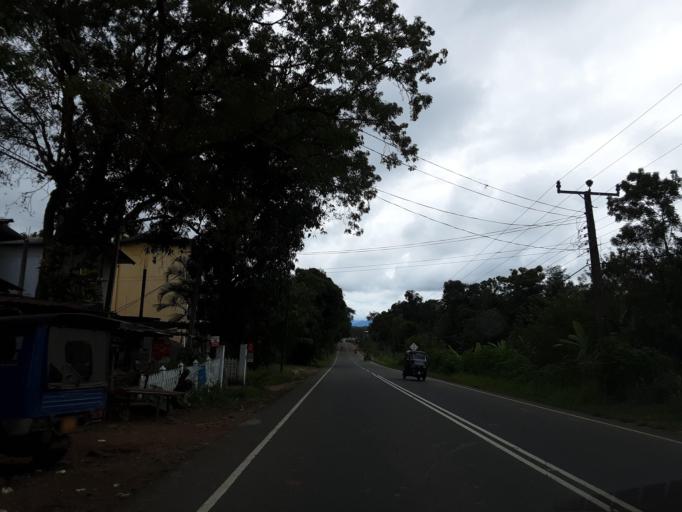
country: LK
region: Uva
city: Badulla
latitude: 7.3810
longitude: 81.0713
